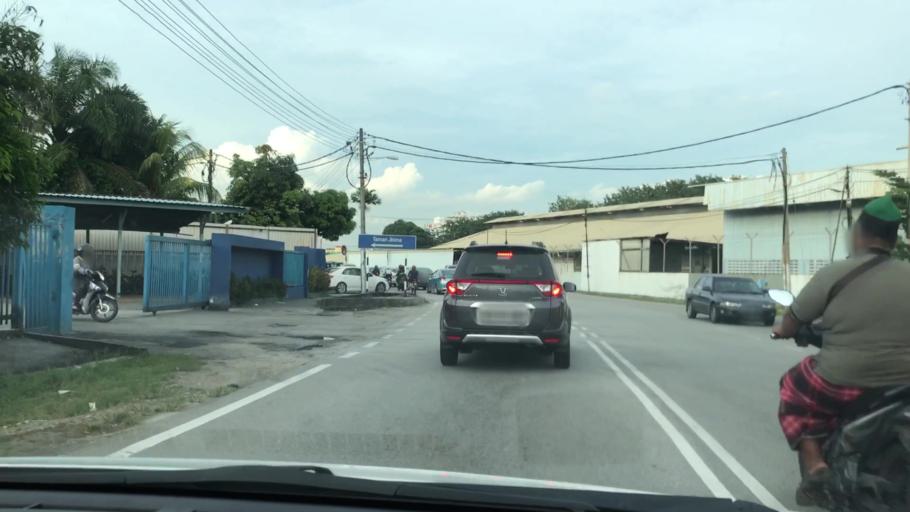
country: MY
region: Selangor
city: Kampong Baharu Balakong
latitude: 3.0151
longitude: 101.7023
